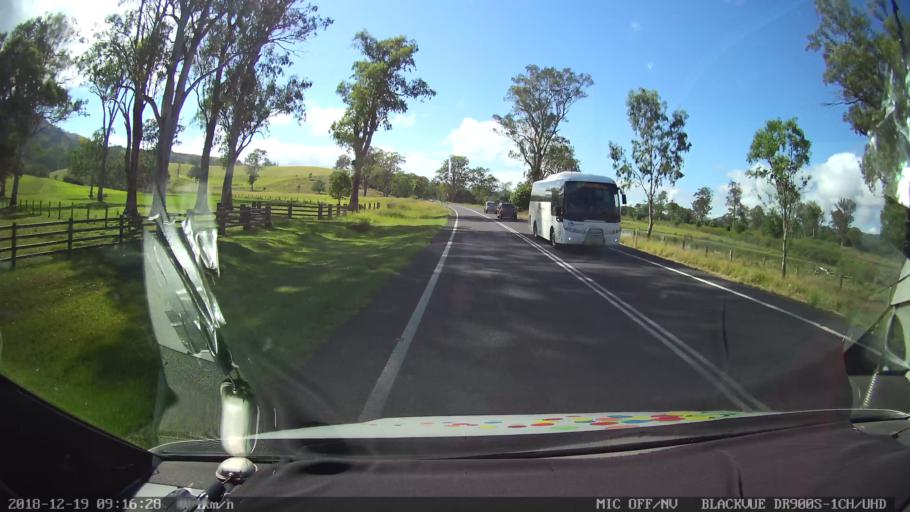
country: AU
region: New South Wales
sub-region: Kyogle
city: Kyogle
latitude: -28.5215
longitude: 152.9675
